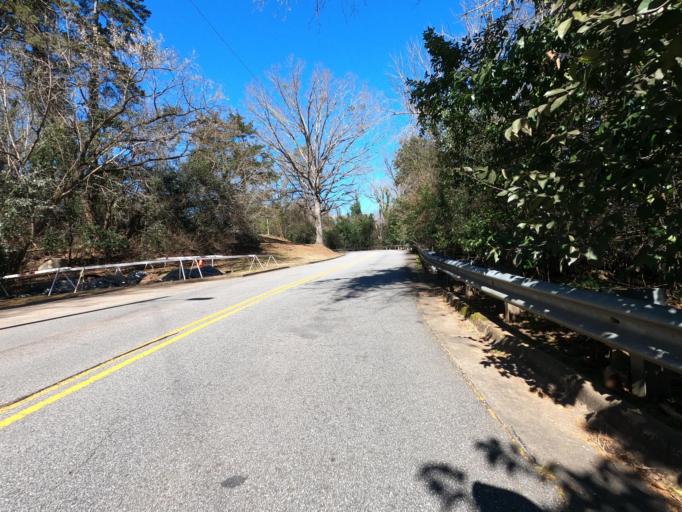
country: US
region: Georgia
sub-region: Clarke County
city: Athens
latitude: 33.9471
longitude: -83.3706
